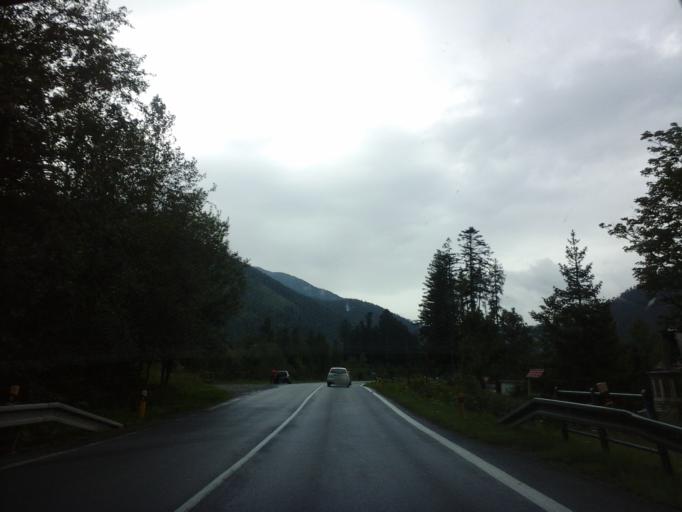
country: SK
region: Presovsky
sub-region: Okres Poprad
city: Zdiar
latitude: 49.2214
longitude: 20.3303
